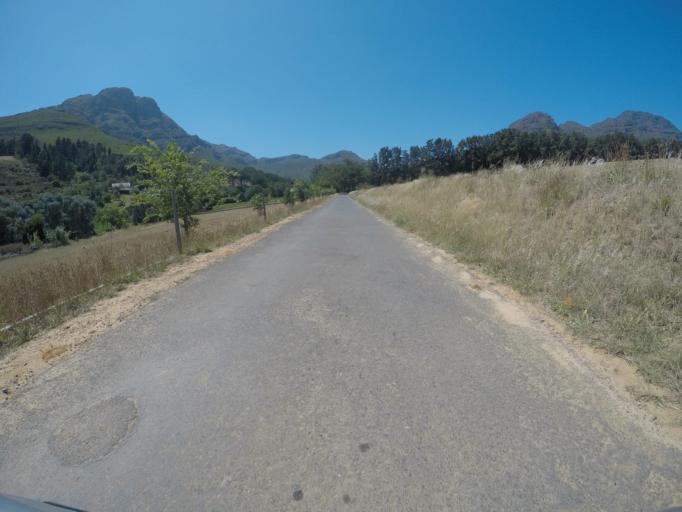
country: ZA
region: Western Cape
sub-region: Cape Winelands District Municipality
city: Stellenbosch
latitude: -34.0020
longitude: 18.8862
